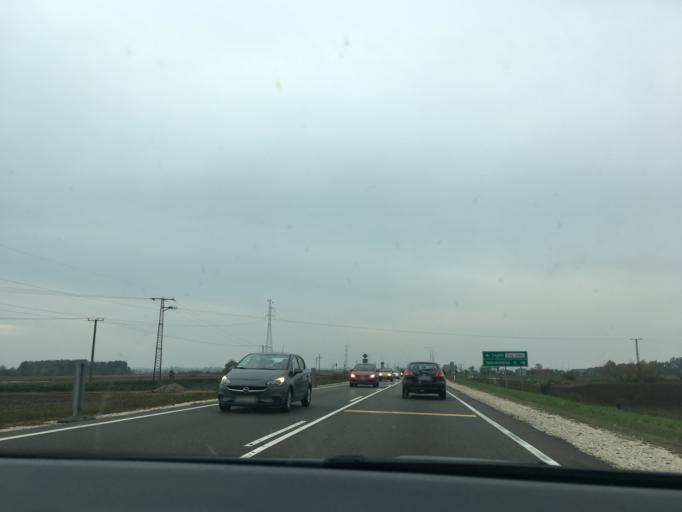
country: HU
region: Pest
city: Cegled
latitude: 47.2014
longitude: 19.7865
